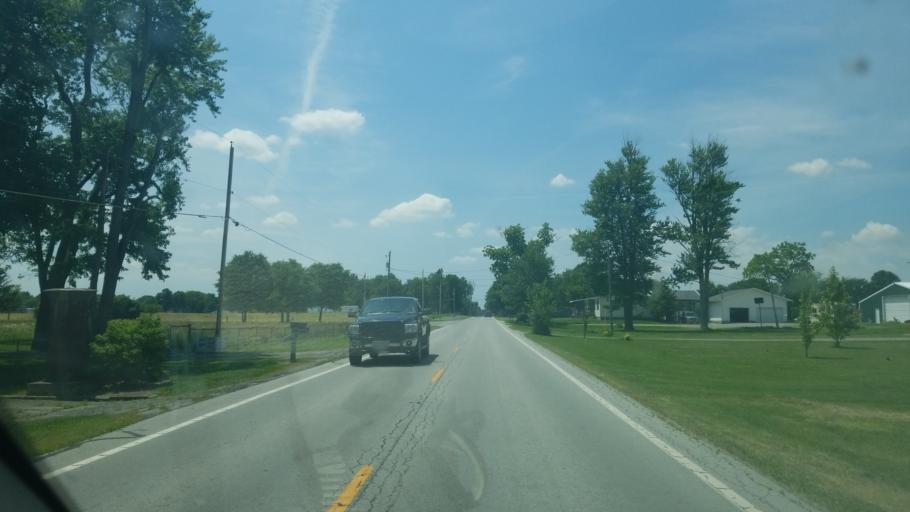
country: US
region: Ohio
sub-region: Hardin County
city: Ada
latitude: 40.7766
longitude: -83.8106
